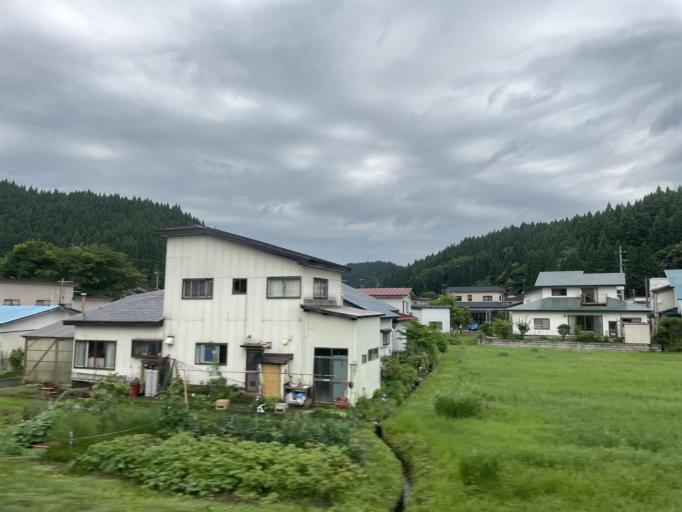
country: JP
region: Akita
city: Takanosu
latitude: 40.2278
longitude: 140.3251
